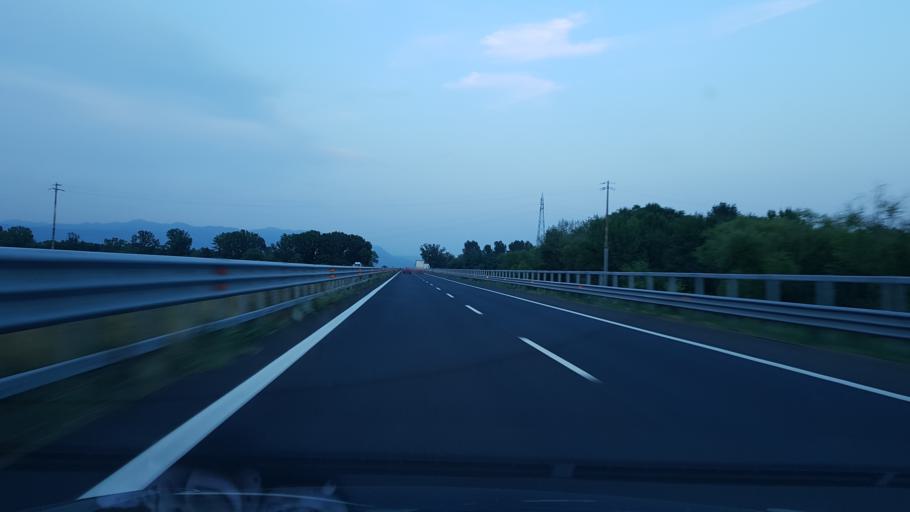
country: IT
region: Friuli Venezia Giulia
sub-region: Provincia di Gorizia
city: Savogna d'Isonzo
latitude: 45.9036
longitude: 13.5500
